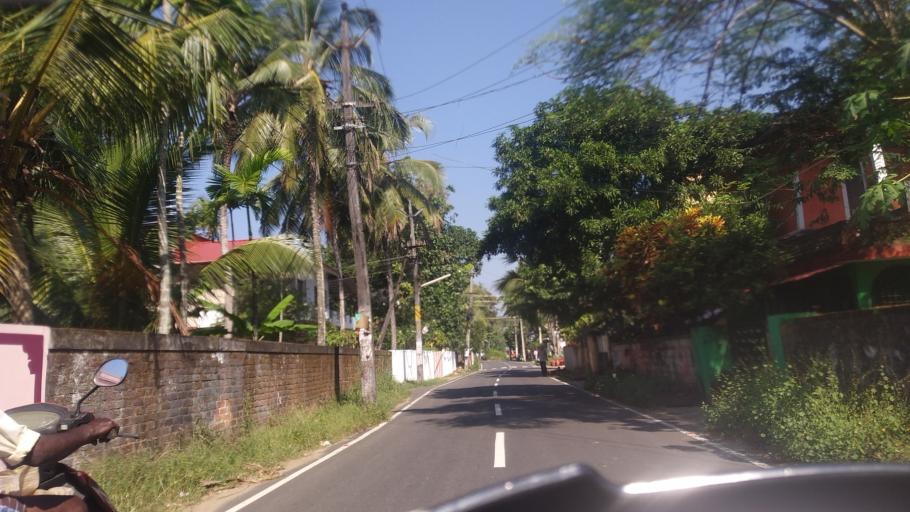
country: IN
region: Kerala
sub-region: Ernakulam
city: Elur
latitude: 10.1151
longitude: 76.2477
